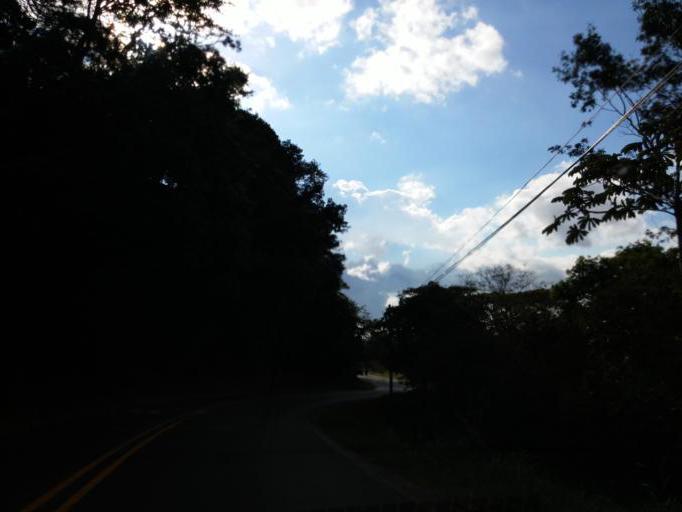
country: CR
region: San Jose
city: San Ignacio
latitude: 9.7963
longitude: -84.1389
